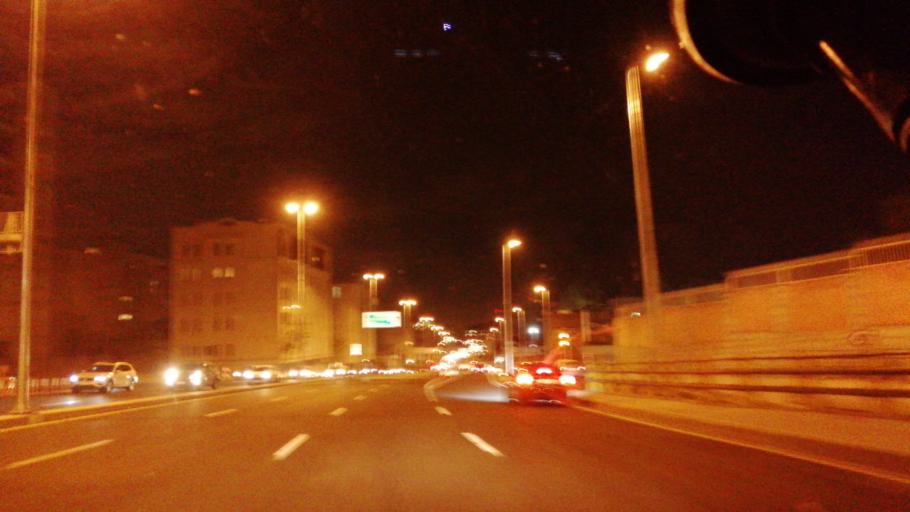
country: IR
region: Tehran
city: Tajrish
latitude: 35.7957
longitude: 51.4897
